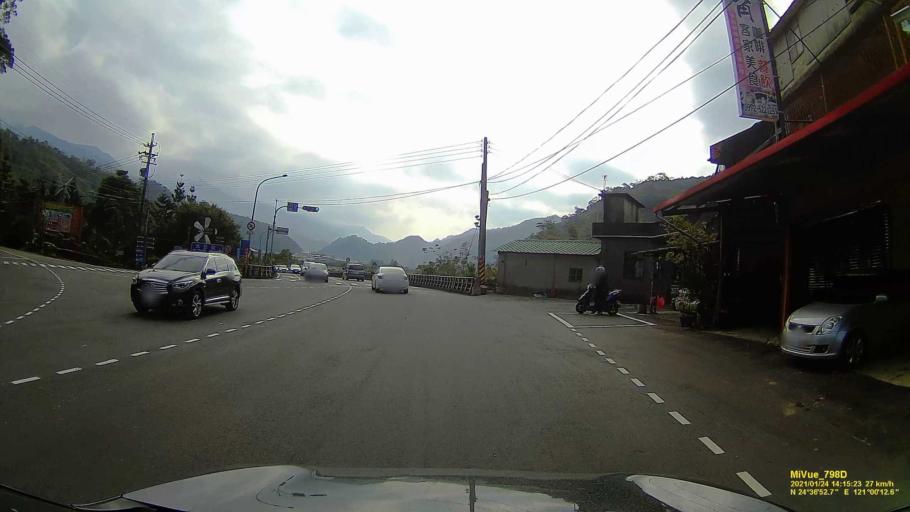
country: TW
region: Taiwan
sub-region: Miaoli
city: Miaoli
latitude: 24.6143
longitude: 121.0034
